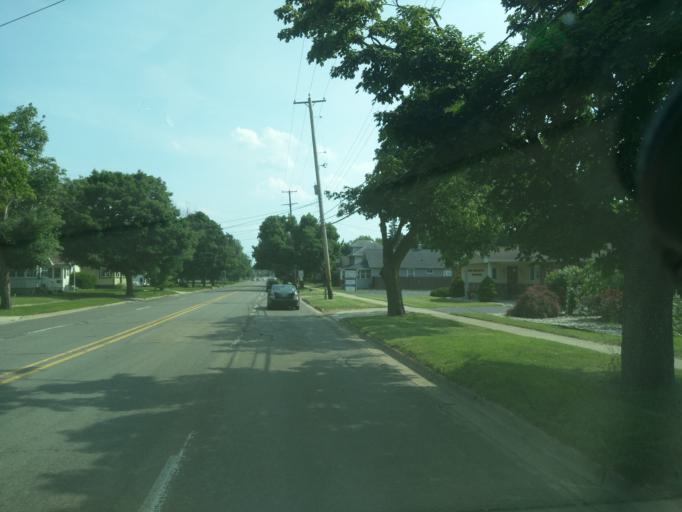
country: US
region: Michigan
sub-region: Jackson County
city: Jackson
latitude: 42.2582
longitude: -84.4284
